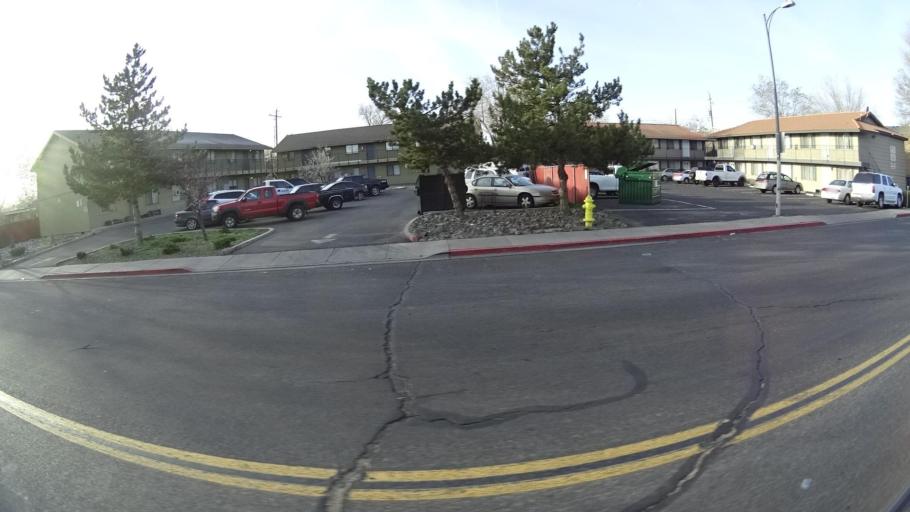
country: US
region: Nevada
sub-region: Washoe County
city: Sparks
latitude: 39.5388
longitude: -119.7781
